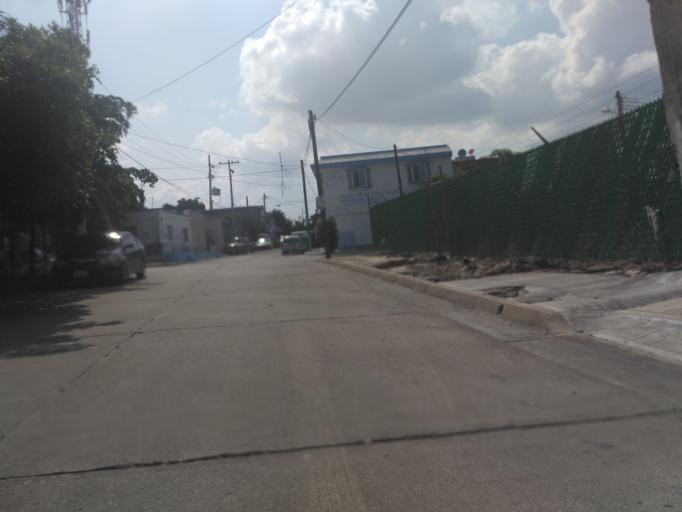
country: MX
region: Sinaloa
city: Culiacan
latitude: 24.7924
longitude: -107.4037
